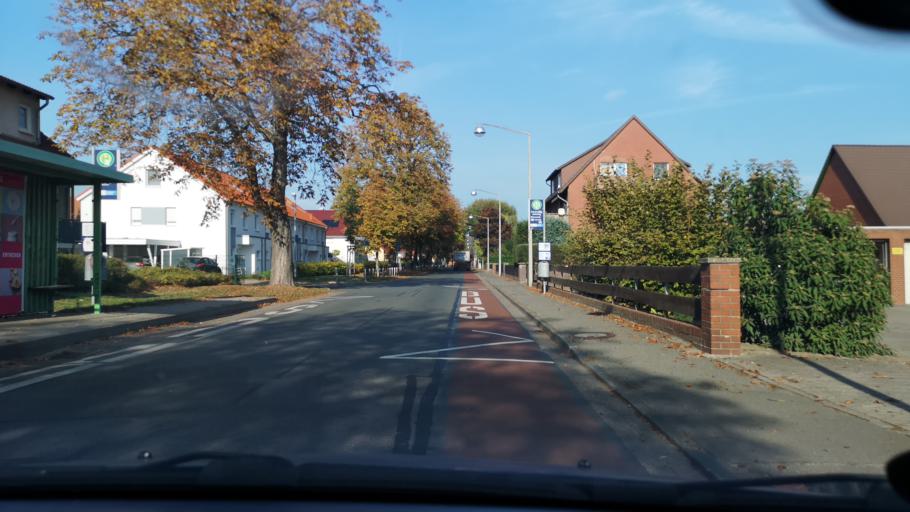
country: DE
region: Lower Saxony
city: Langenhagen
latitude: 52.4427
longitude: 9.6746
